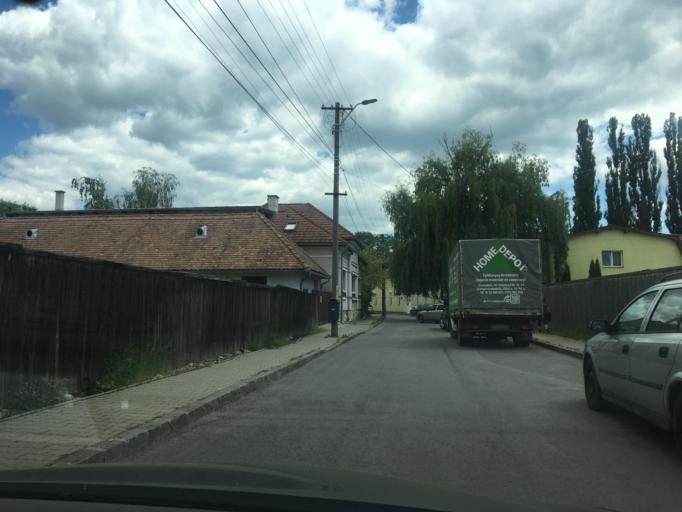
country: RO
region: Harghita
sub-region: Municipiul Gheorgheni
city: Gheorgheni
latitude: 46.7223
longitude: 25.6044
